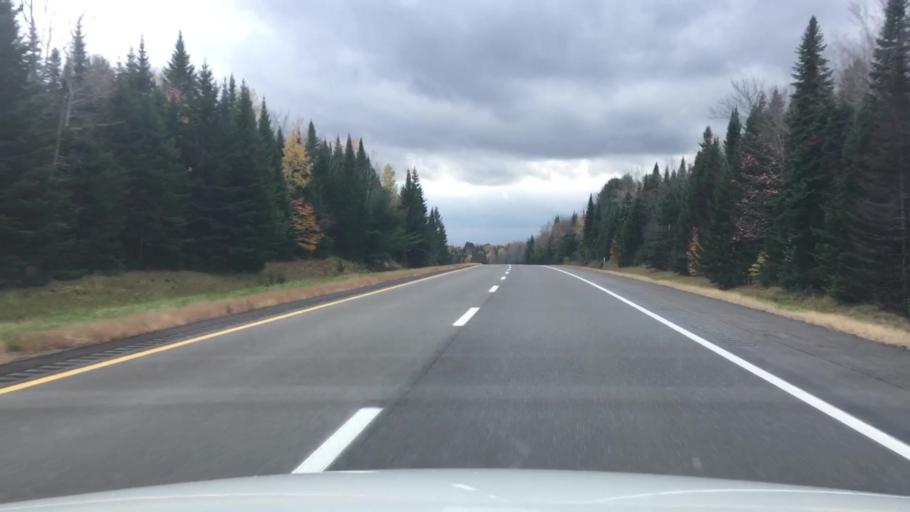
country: US
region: Maine
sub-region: Penobscot County
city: Patten
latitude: 46.0900
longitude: -68.2032
